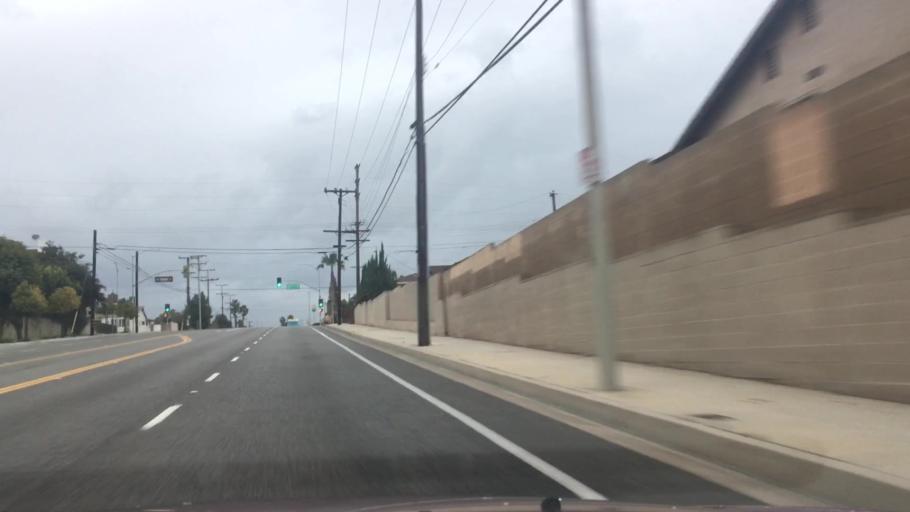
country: US
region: California
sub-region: Los Angeles County
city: East La Mirada
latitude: 33.9236
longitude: -117.9944
